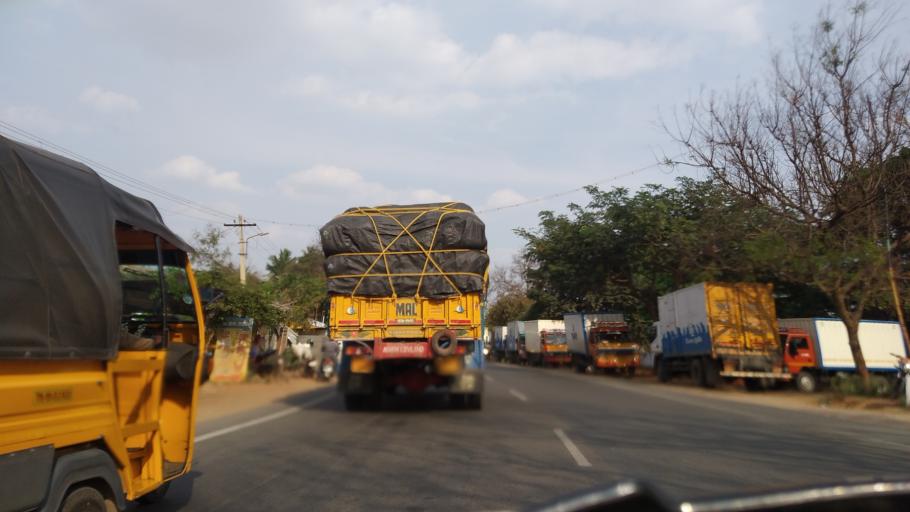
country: IN
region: Tamil Nadu
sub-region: Coimbatore
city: Perur
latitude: 10.9676
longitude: 76.9029
